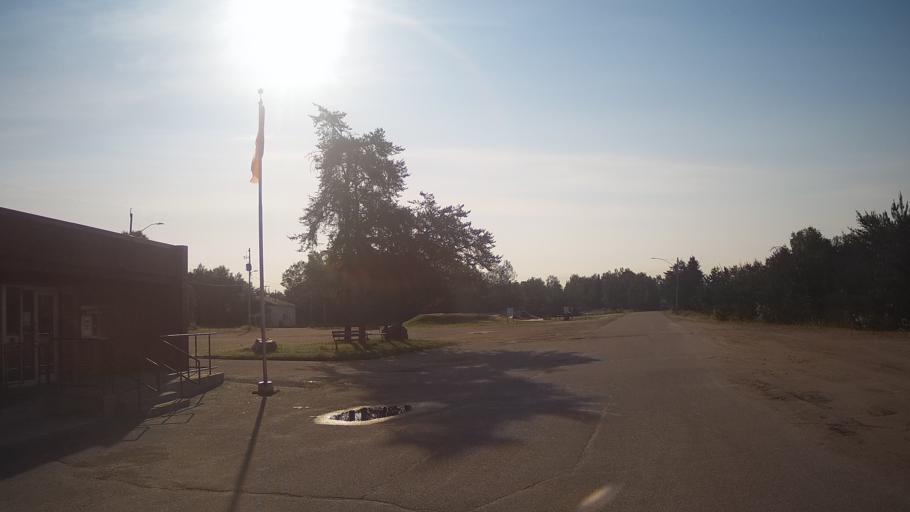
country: CA
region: Ontario
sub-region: Rainy River District
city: Atikokan
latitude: 49.4152
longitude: -91.6650
